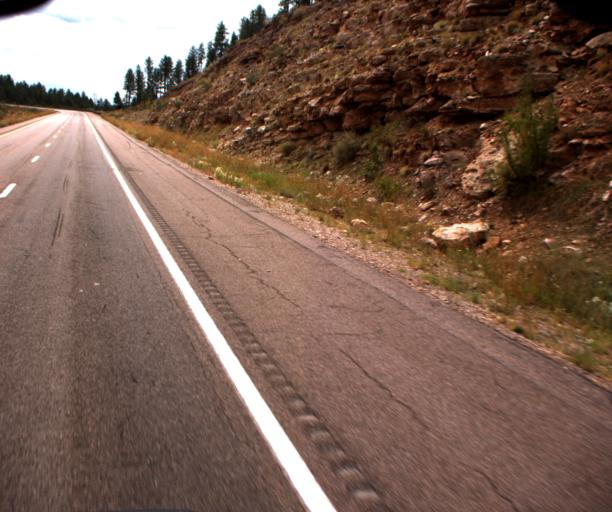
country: US
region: Arizona
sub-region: Gila County
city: Star Valley
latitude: 34.3112
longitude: -111.0260
